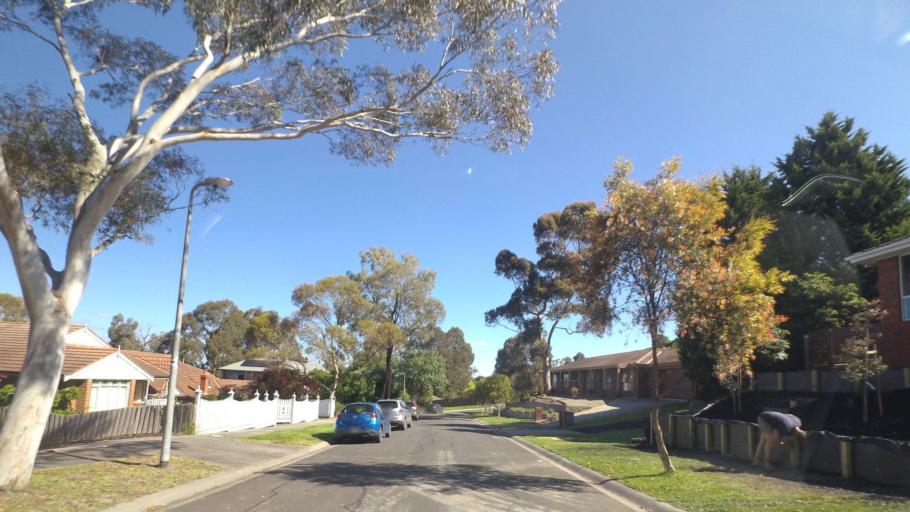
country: AU
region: Victoria
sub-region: Maroondah
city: Heathmont
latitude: -37.8266
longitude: 145.2533
